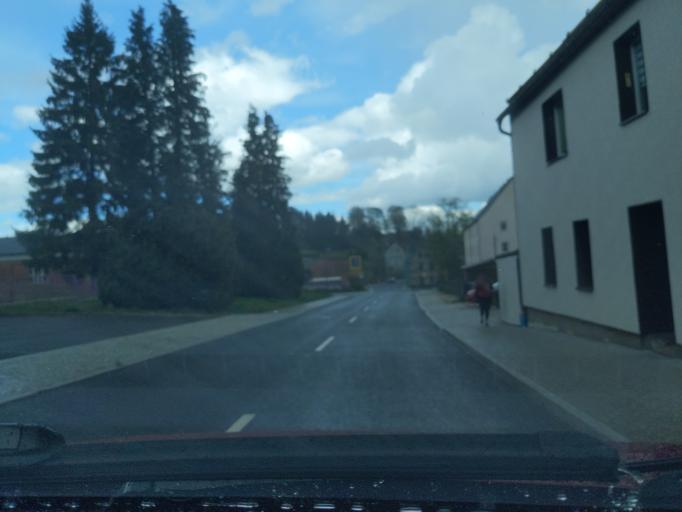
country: DE
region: Saxony
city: Schoenheide
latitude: 50.5041
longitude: 12.5080
